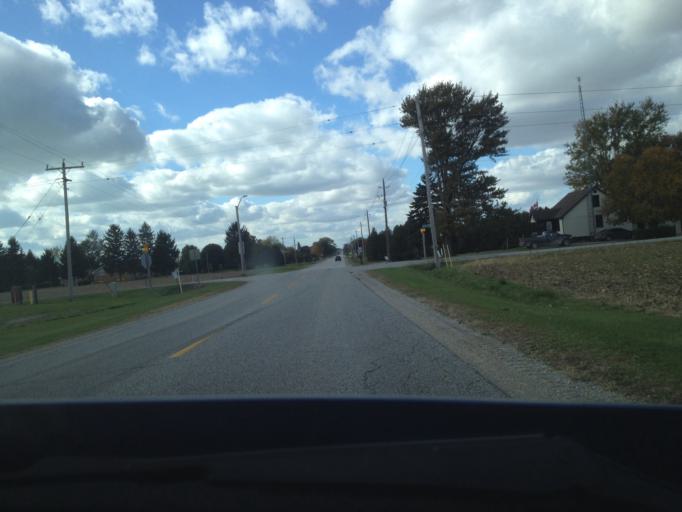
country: CA
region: Ontario
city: Amherstburg
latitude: 42.0322
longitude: -82.5558
